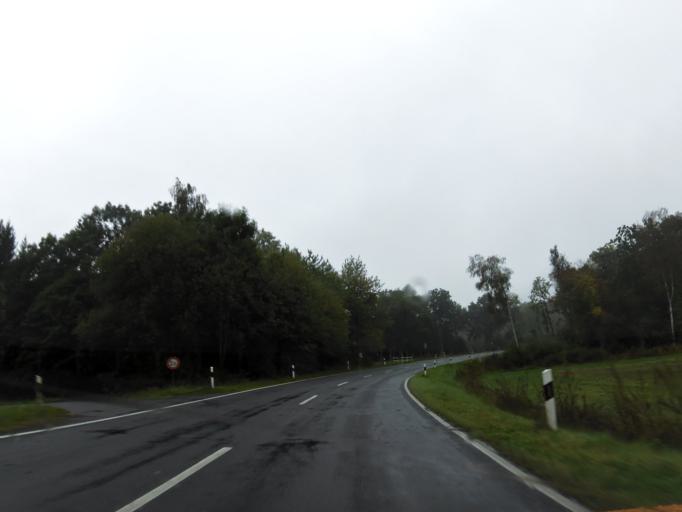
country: DE
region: Lower Saxony
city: Walkenried
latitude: 51.5981
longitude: 10.6021
